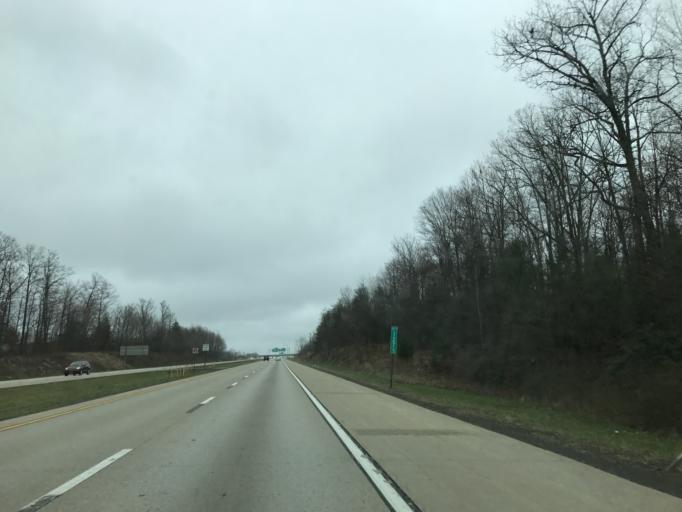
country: US
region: West Virginia
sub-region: Raleigh County
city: Daniels
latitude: 37.7735
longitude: -81.0787
